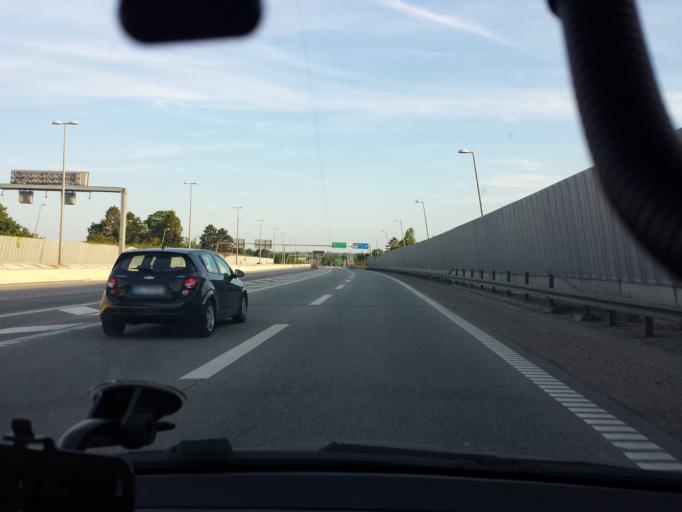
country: DK
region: Capital Region
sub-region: Herlev Kommune
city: Herlev
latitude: 55.7370
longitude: 12.4545
